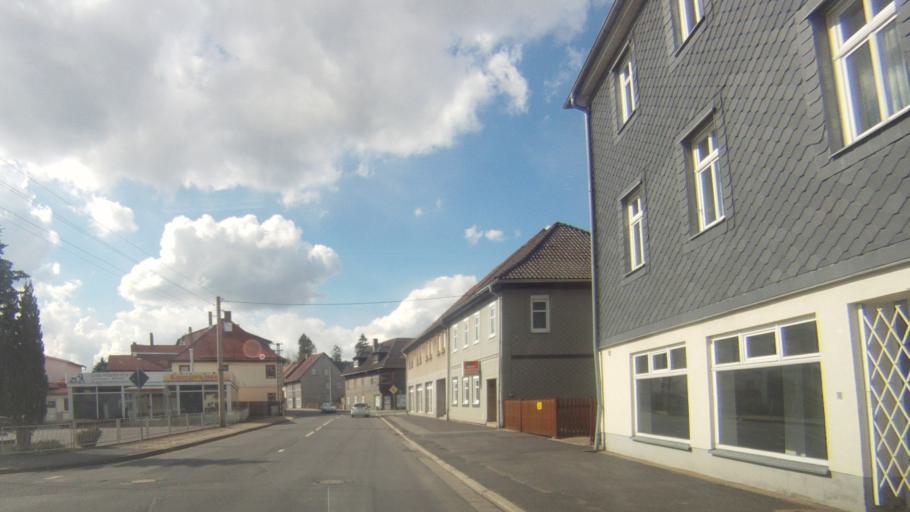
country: DE
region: Thuringia
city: Eisfeld
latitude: 50.4266
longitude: 10.9048
